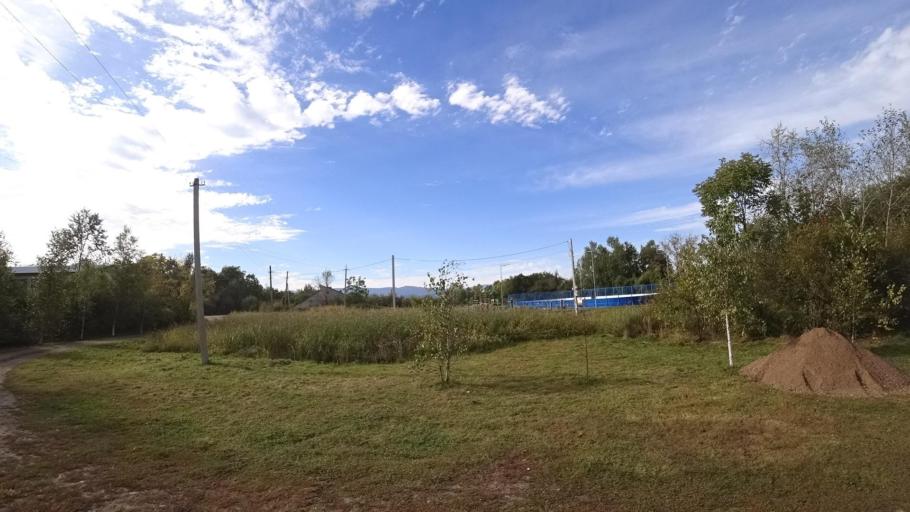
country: RU
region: Primorskiy
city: Dostoyevka
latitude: 44.2986
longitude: 133.4563
